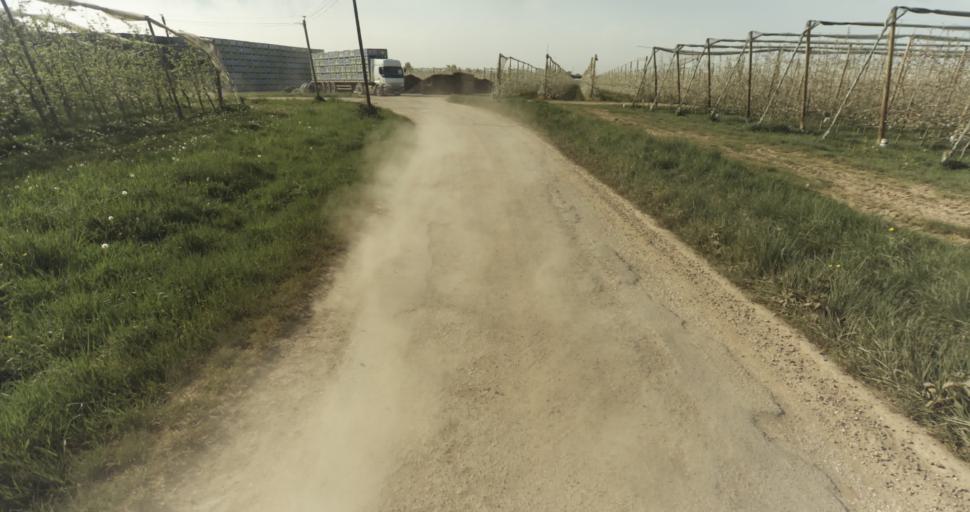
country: FR
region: Midi-Pyrenees
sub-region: Departement du Tarn-et-Garonne
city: Moissac
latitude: 44.1021
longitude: 1.1191
